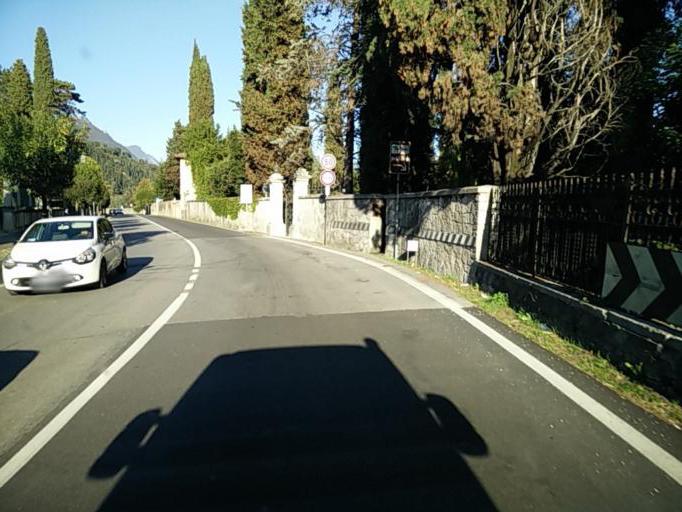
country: IT
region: Lombardy
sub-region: Provincia di Brescia
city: Gardone Riviera
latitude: 45.6263
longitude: 10.5853
